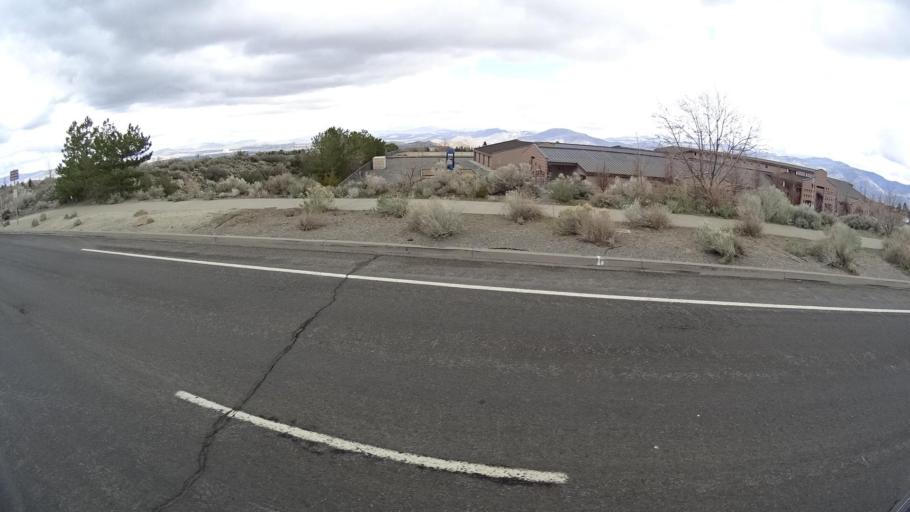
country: US
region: Nevada
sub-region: Washoe County
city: Reno
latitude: 39.4061
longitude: -119.8022
